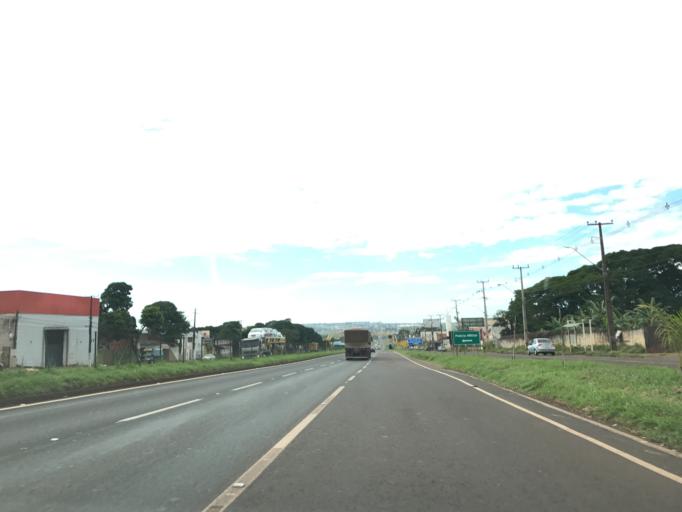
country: BR
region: Parana
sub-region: Sarandi
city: Sarandi
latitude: -23.4433
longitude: -51.8683
